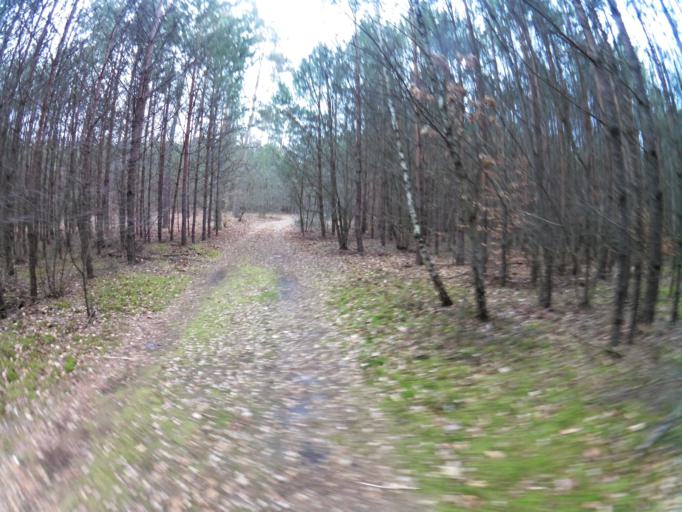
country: PL
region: West Pomeranian Voivodeship
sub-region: Powiat mysliborski
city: Debno
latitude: 52.7226
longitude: 14.7351
